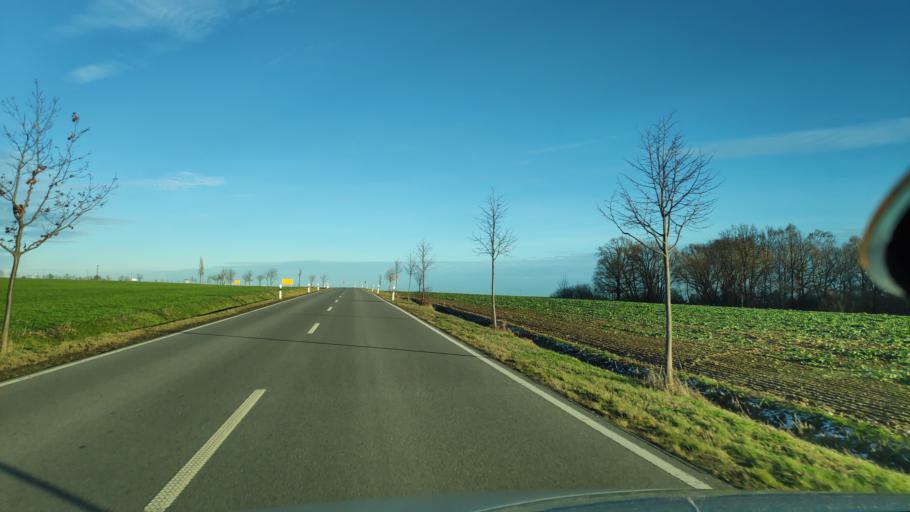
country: DE
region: Thuringia
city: Seelingstadt
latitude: 50.7988
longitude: 12.2572
